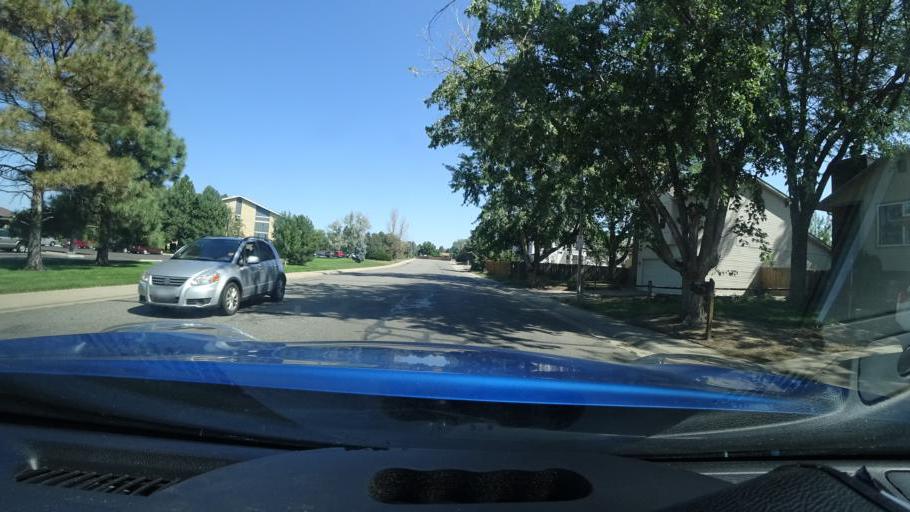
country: US
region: Colorado
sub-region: Adams County
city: Aurora
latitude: 39.6877
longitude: -104.8235
